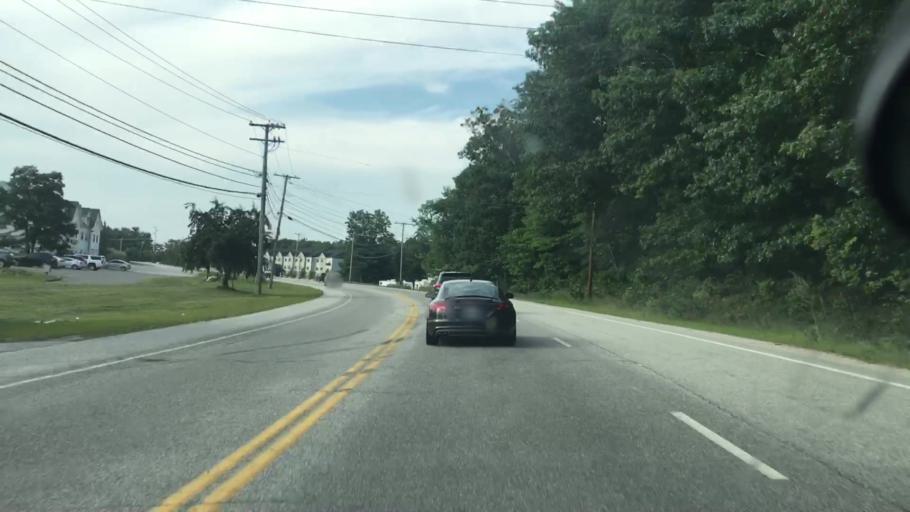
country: US
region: Maine
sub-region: Cumberland County
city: North Windham
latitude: 43.8544
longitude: -70.4512
